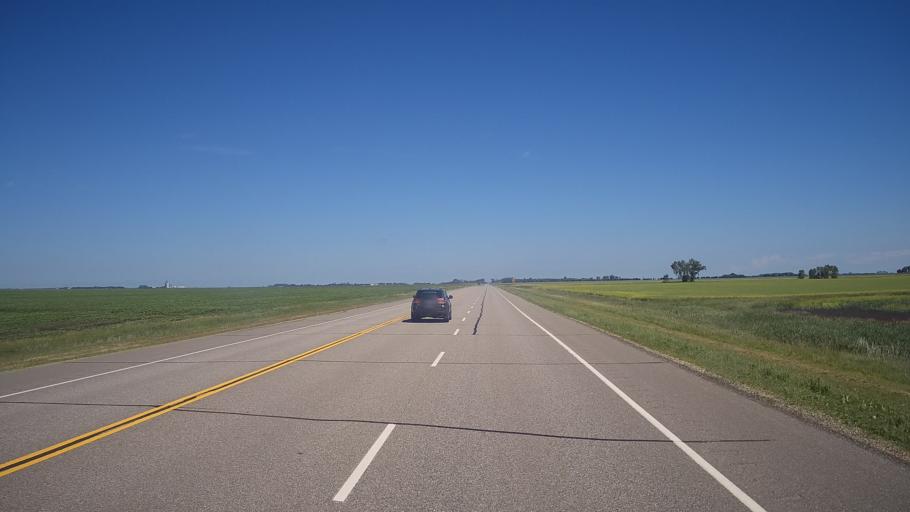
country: CA
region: Manitoba
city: Portage la Prairie
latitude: 50.0260
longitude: -98.4686
